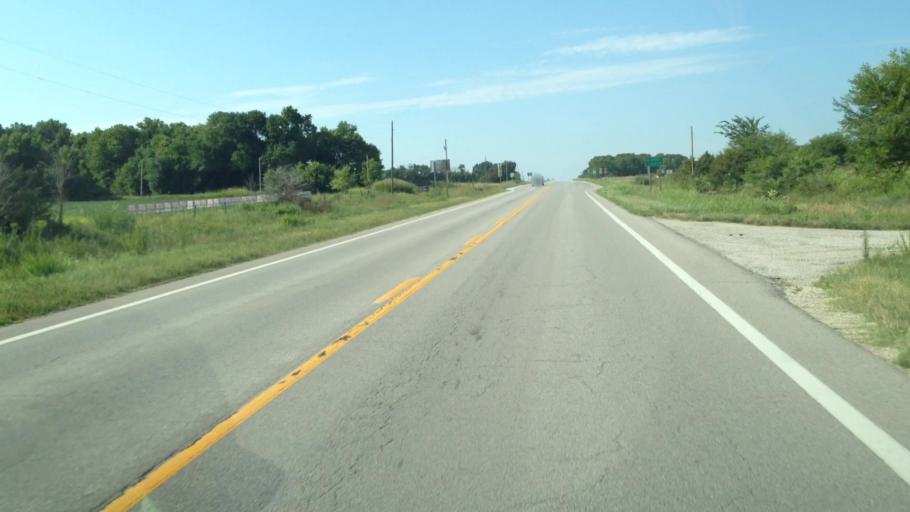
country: US
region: Kansas
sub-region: Neosho County
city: Erie
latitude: 37.7179
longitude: -95.1607
